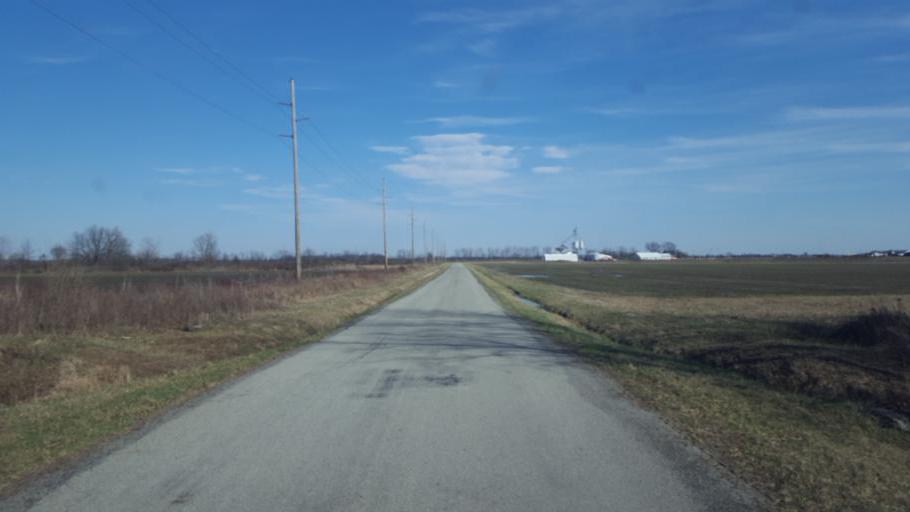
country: US
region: Ohio
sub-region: Wyandot County
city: Upper Sandusky
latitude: 40.6943
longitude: -83.3069
